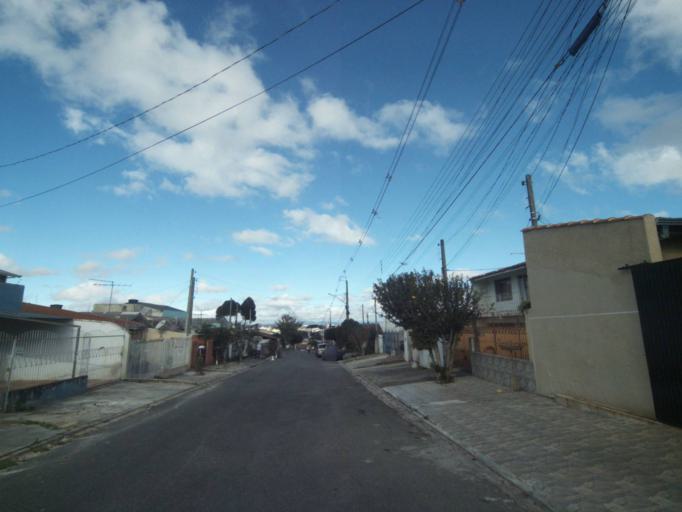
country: BR
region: Parana
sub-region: Sao Jose Dos Pinhais
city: Sao Jose dos Pinhais
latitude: -25.5311
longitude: -49.2842
